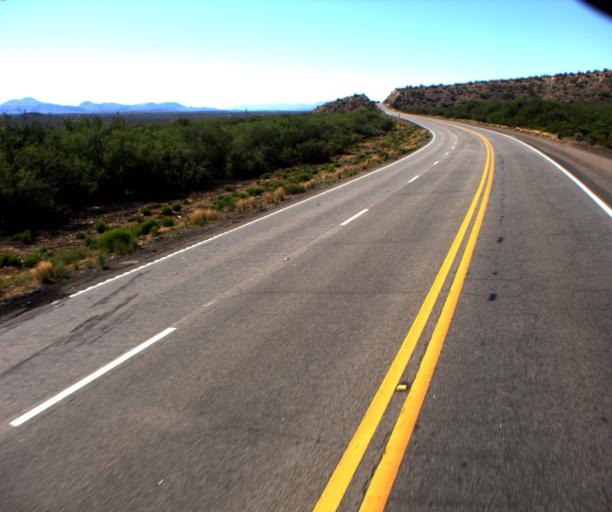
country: US
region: Arizona
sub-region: Yavapai County
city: Bagdad
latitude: 34.8030
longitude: -113.6259
